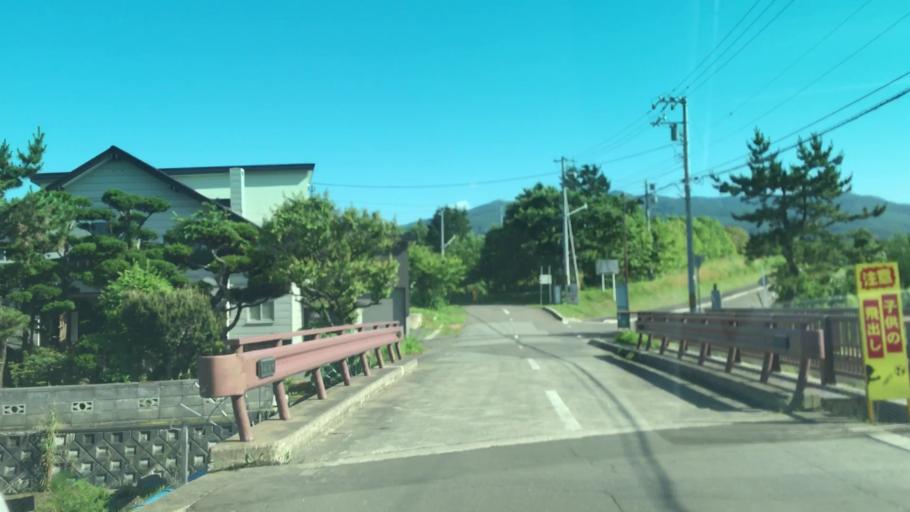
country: JP
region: Hokkaido
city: Iwanai
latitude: 42.9793
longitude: 140.6086
